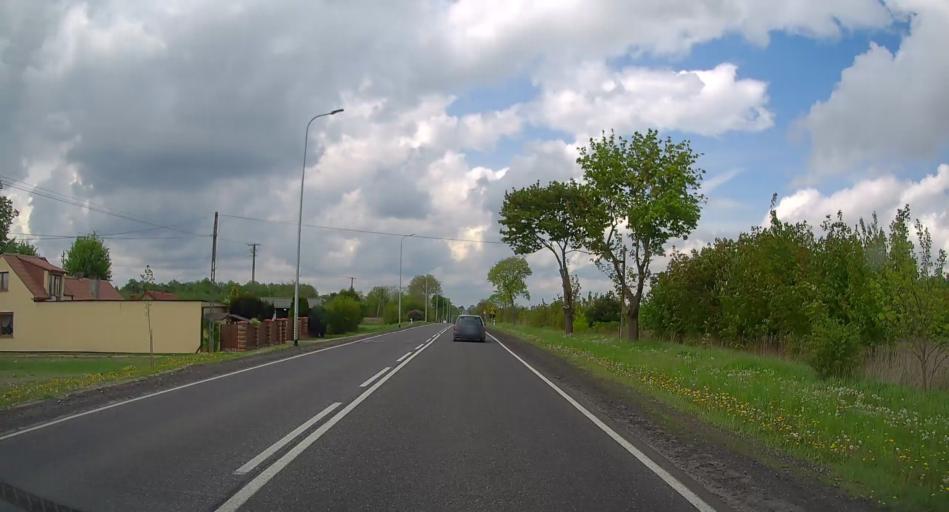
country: PL
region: Masovian Voivodeship
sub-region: Powiat nowodworski
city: Zakroczym
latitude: 52.4412
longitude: 20.5509
